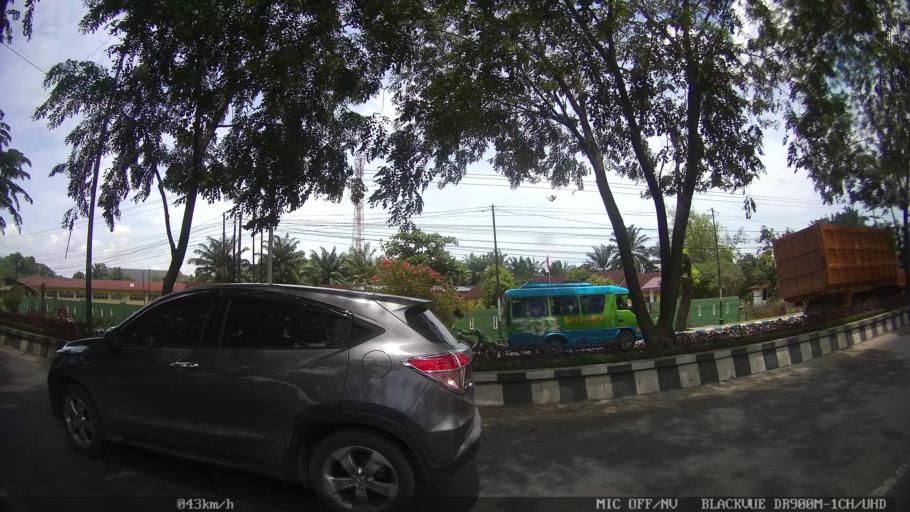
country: ID
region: North Sumatra
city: Percut
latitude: 3.5525
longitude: 98.8697
